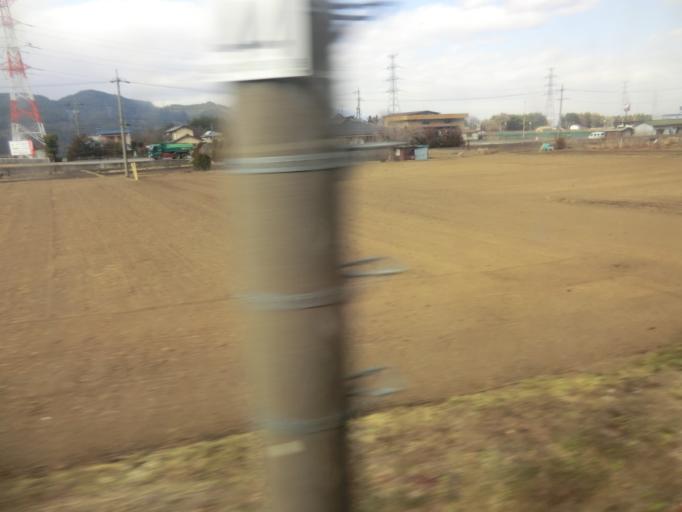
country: JP
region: Nagano
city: Shiojiri
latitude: 36.0937
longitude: 137.9238
